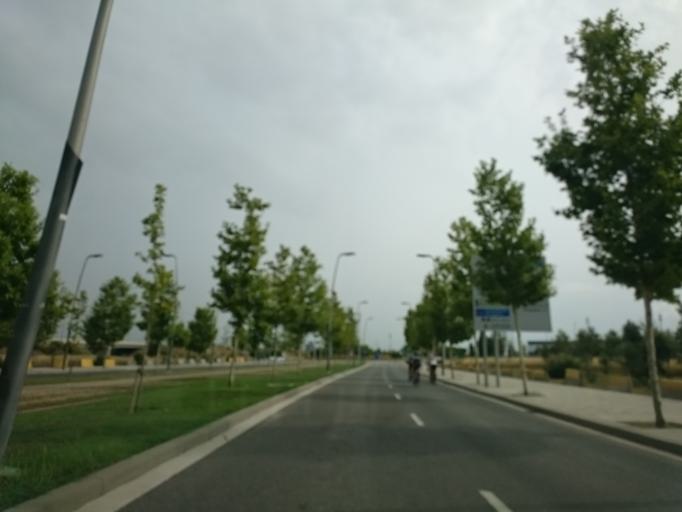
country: ES
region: Catalonia
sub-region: Provincia de Barcelona
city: Viladecans
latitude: 41.2977
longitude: 2.0530
